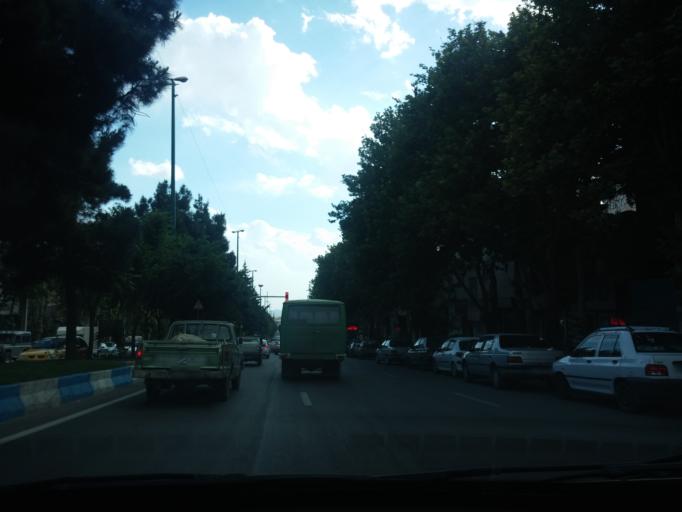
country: IR
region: Tehran
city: Damavand
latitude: 35.7343
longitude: 51.9076
